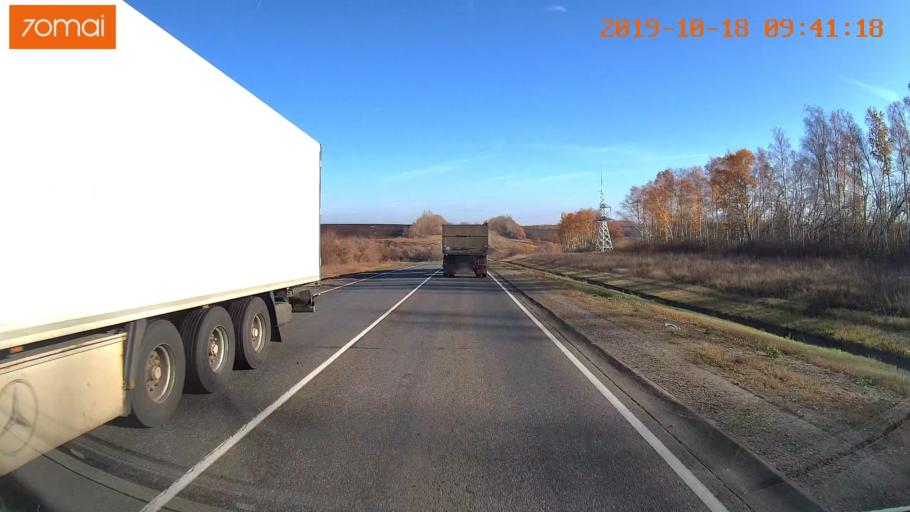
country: RU
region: Tula
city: Kazachka
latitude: 53.2735
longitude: 38.1600
